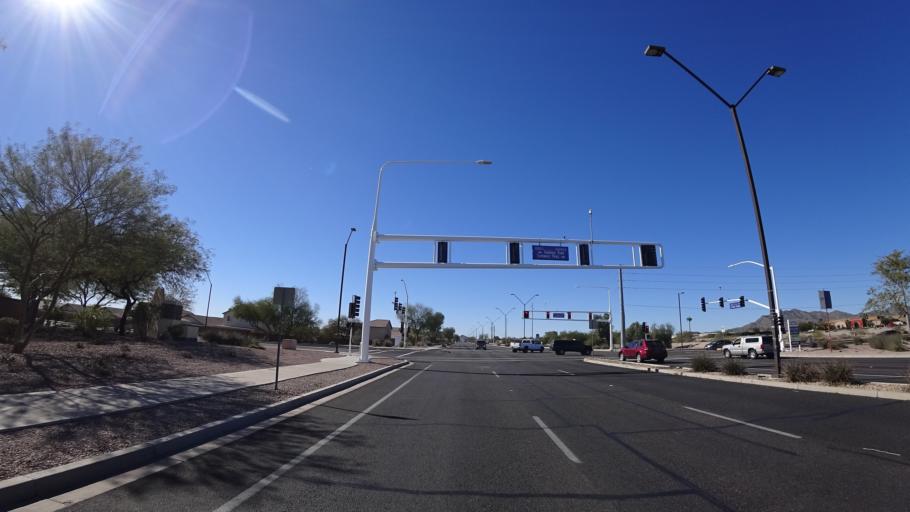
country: US
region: Arizona
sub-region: Maricopa County
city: Buckeye
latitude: 33.4356
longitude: -112.5385
